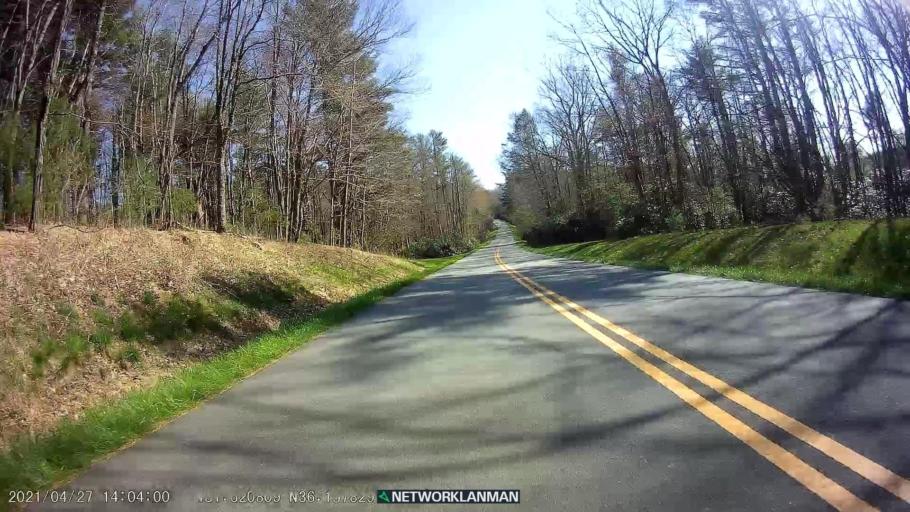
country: US
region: North Carolina
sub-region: Watauga County
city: Blowing Rock
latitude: 36.1580
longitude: -81.6207
